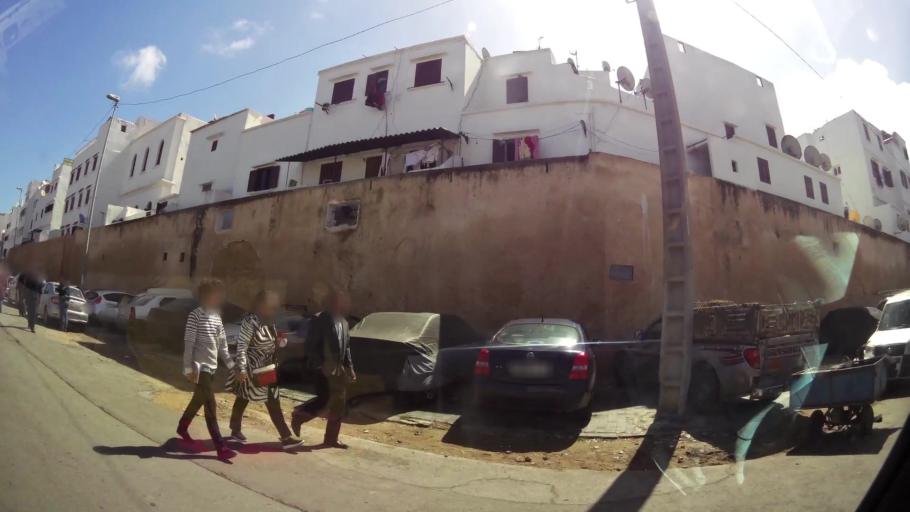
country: MA
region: Grand Casablanca
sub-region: Casablanca
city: Casablanca
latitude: 33.6032
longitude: -7.6227
